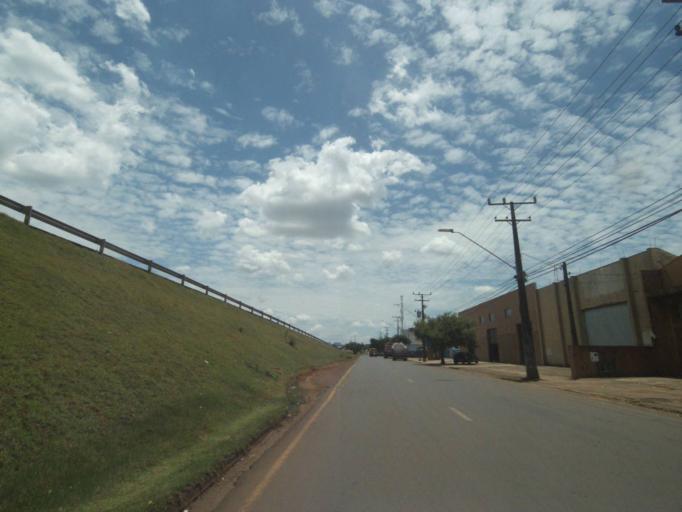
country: BR
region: Parana
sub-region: Londrina
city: Londrina
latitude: -23.3687
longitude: -51.1410
